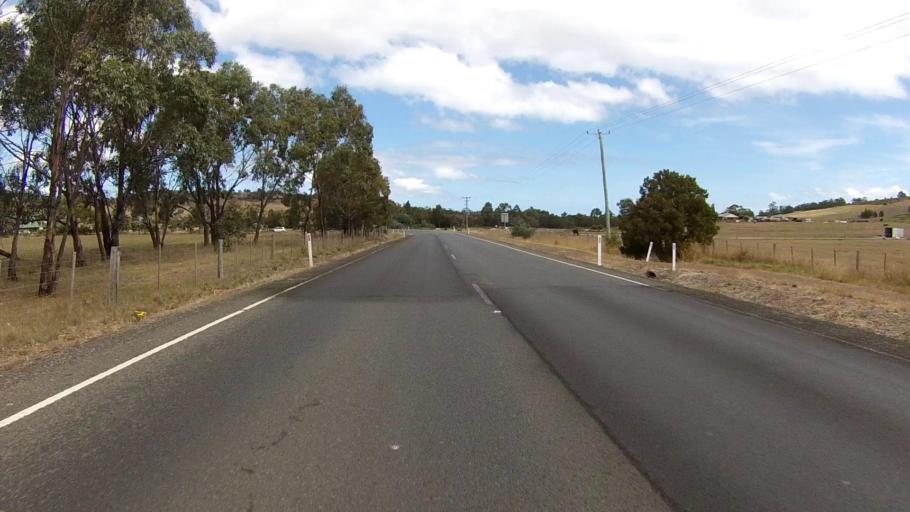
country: AU
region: Tasmania
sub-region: Sorell
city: Sorell
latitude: -42.8292
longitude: 147.6235
